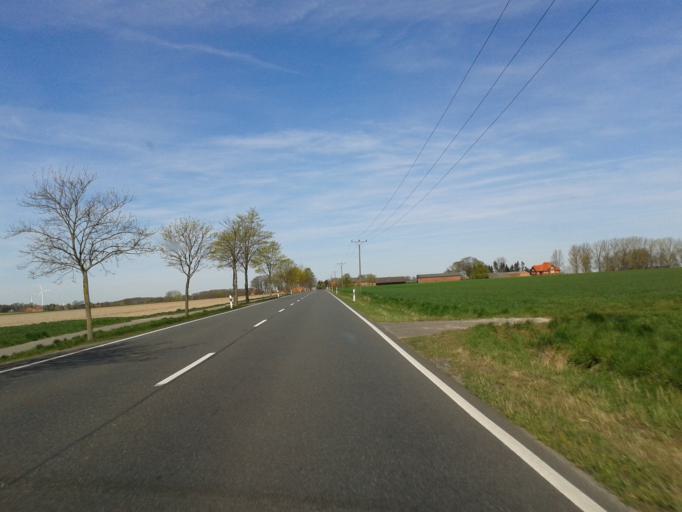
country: DE
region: Lower Saxony
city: Ratzlingen
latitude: 52.9528
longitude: 10.6975
